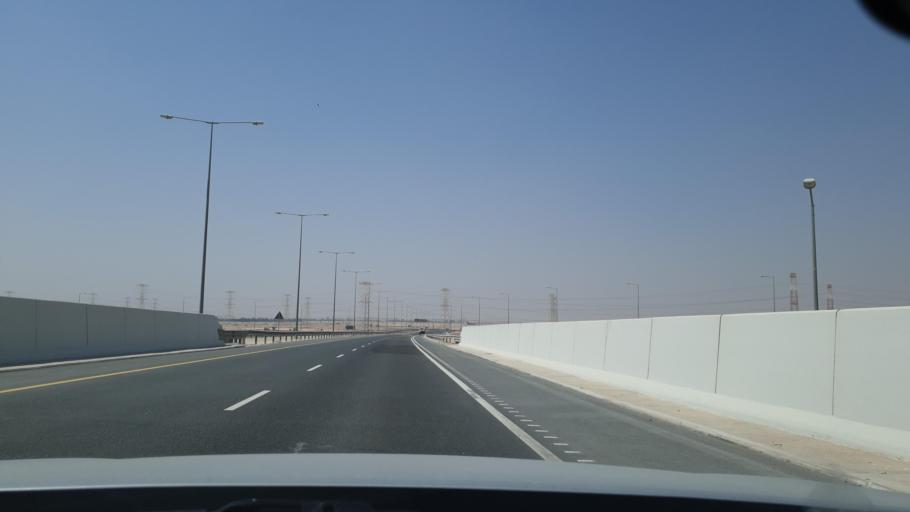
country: QA
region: Baladiyat az Za`ayin
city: Az Za`ayin
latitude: 25.6173
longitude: 51.3649
